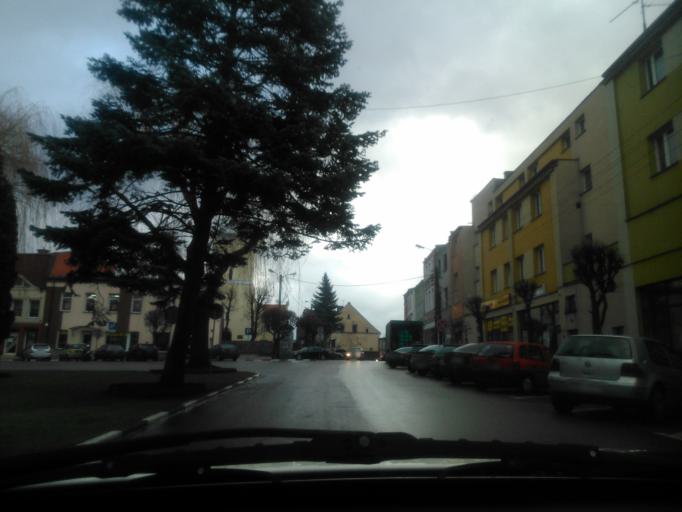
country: PL
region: Warmian-Masurian Voivodeship
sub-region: Powiat dzialdowski
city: Lidzbark
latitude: 53.2629
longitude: 19.8219
